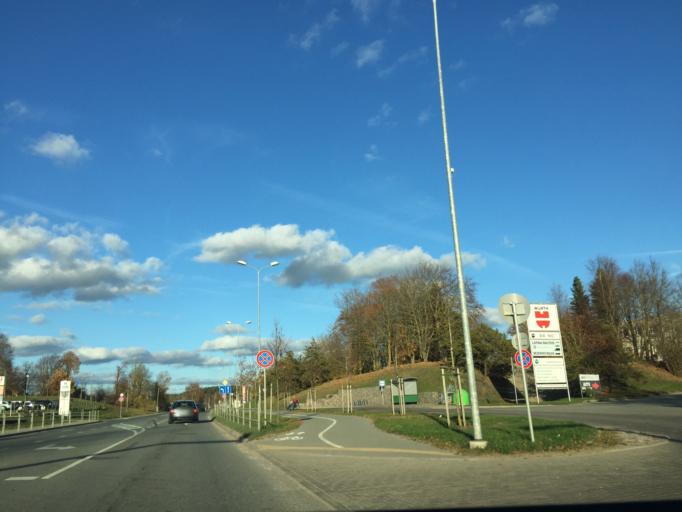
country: LV
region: Tukuma Rajons
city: Tukums
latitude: 56.9522
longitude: 23.1168
